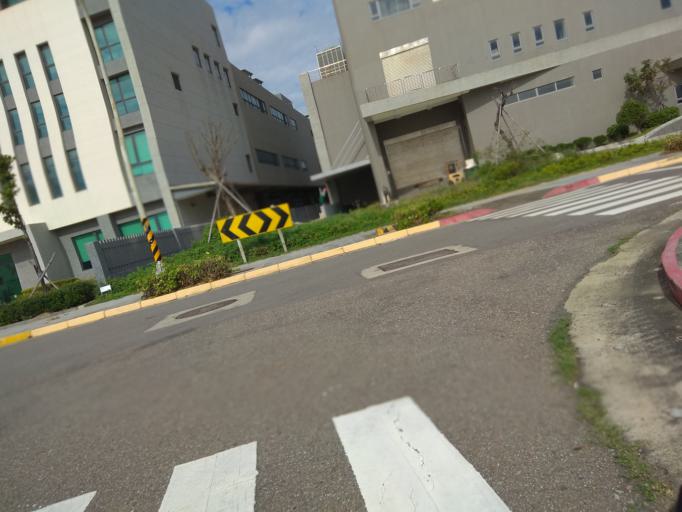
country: TW
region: Taiwan
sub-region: Hsinchu
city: Zhubei
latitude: 25.0376
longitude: 121.0696
